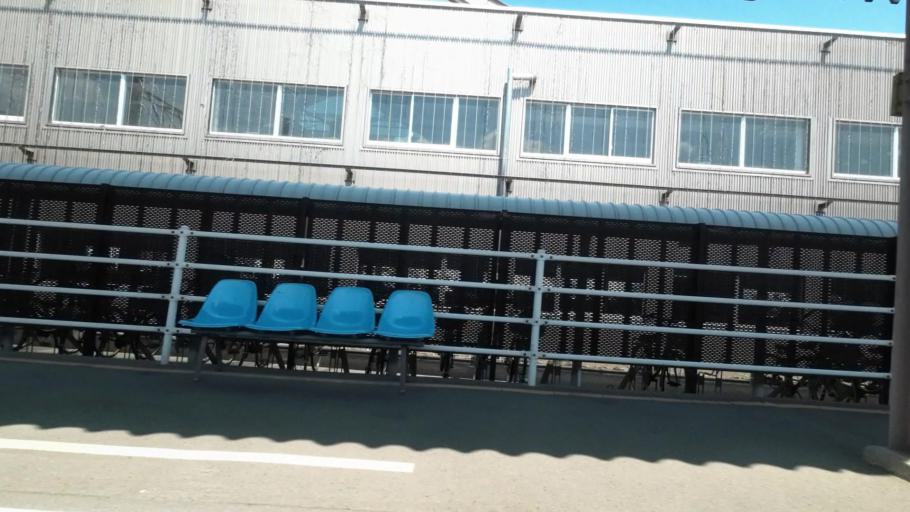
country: JP
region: Ehime
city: Niihama
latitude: 33.9482
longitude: 133.2949
